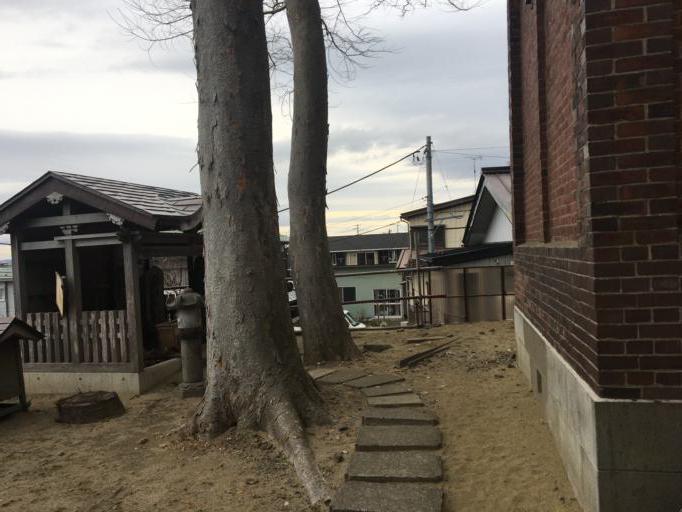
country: JP
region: Aomori
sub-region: Hachinohe Shi
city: Uchimaru
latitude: 40.5252
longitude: 141.5225
